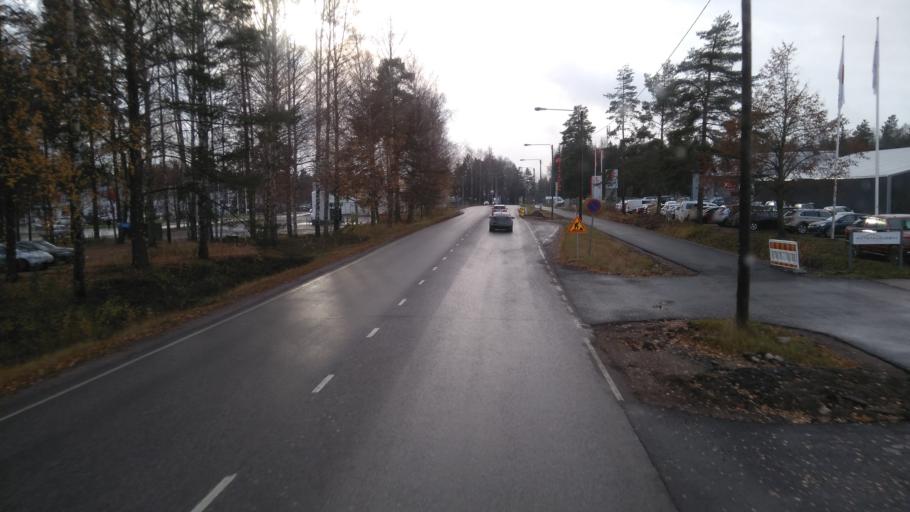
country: FI
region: Uusimaa
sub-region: Porvoo
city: Porvoo
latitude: 60.4024
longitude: 25.6874
